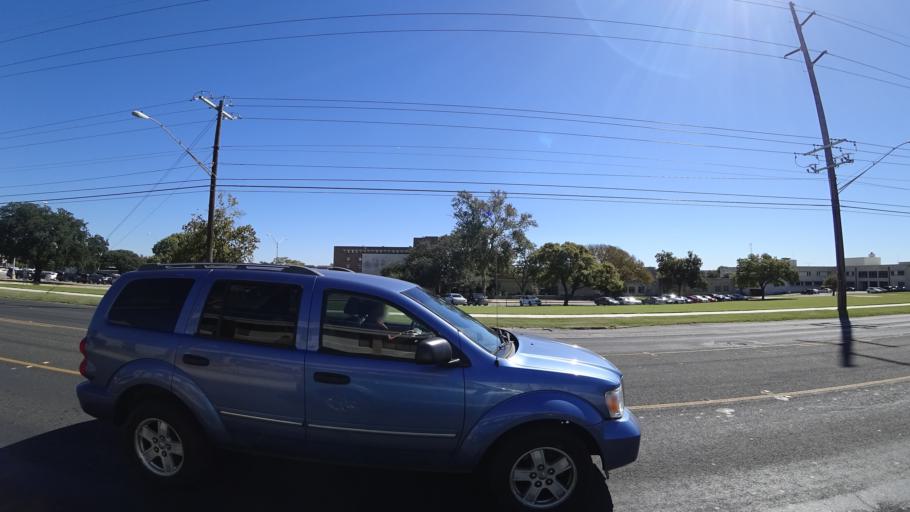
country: US
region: Texas
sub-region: Travis County
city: Austin
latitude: 30.3287
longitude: -97.7246
